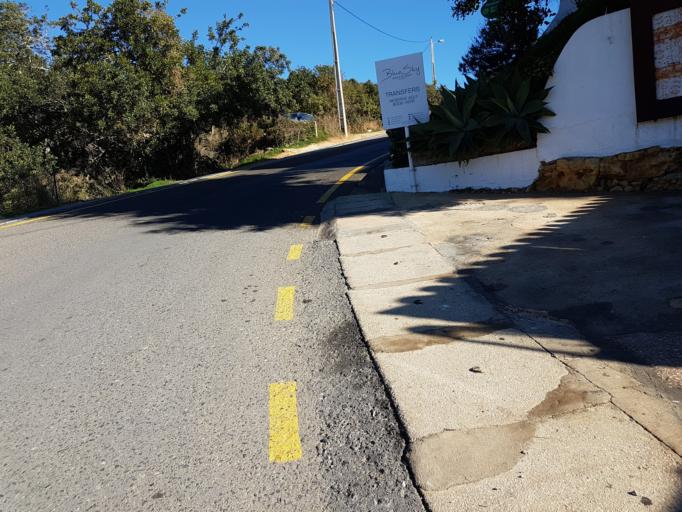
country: PT
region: Faro
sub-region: Lagoa
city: Carvoeiro
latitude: 37.0887
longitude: -8.4265
